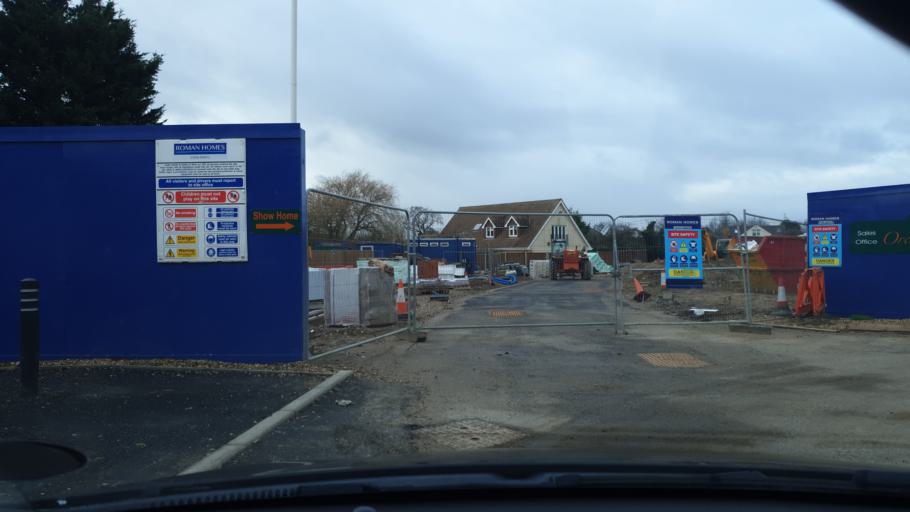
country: GB
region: England
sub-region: Essex
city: Frinton-on-Sea
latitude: 51.8428
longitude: 1.2226
